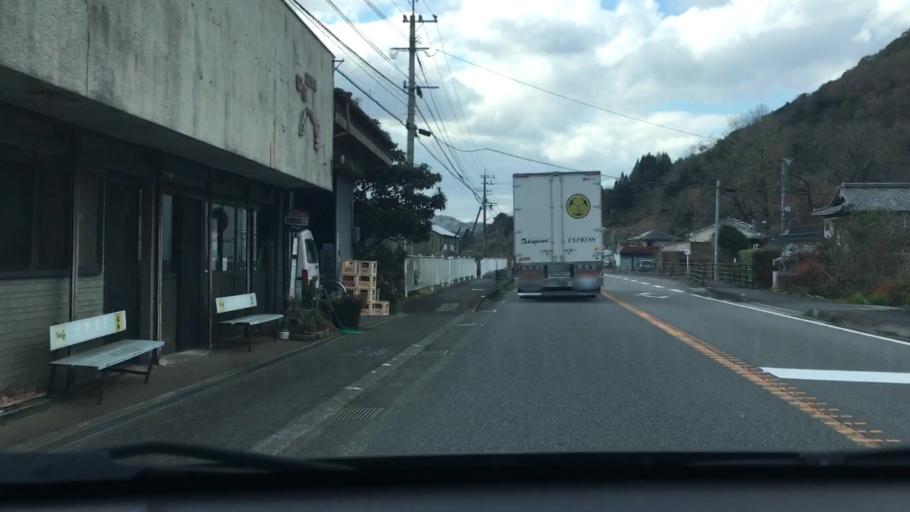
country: JP
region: Oita
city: Usuki
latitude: 33.0051
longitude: 131.7345
